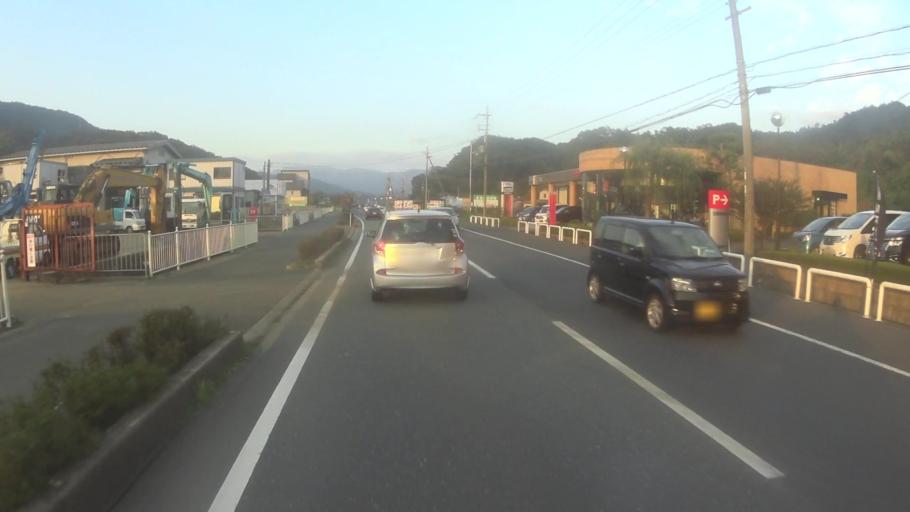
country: JP
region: Kyoto
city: Miyazu
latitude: 35.5427
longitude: 135.1326
